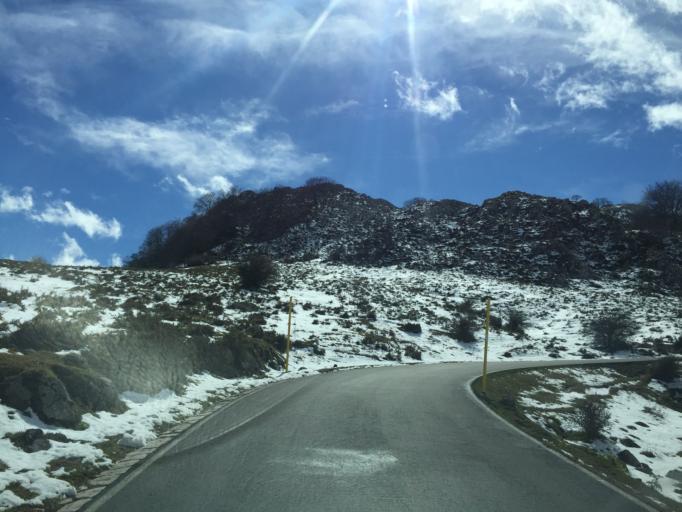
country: ES
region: Asturias
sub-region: Province of Asturias
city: Amieva
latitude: 43.2811
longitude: -5.0029
